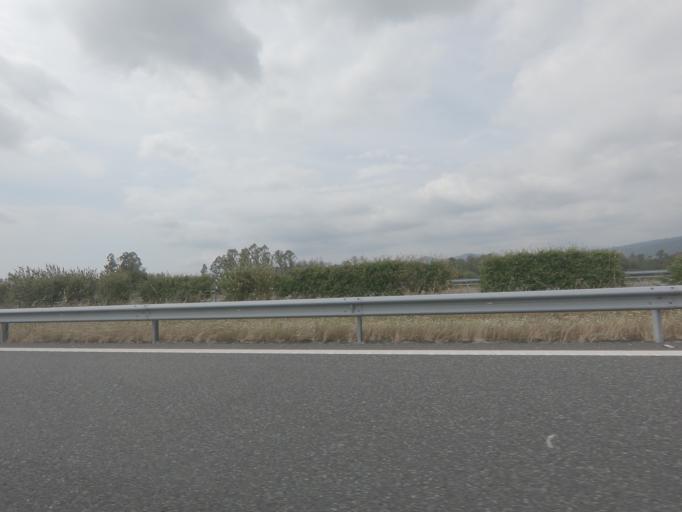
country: ES
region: Galicia
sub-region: Provincia de Pontevedra
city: Ponteareas
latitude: 42.1429
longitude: -8.4646
